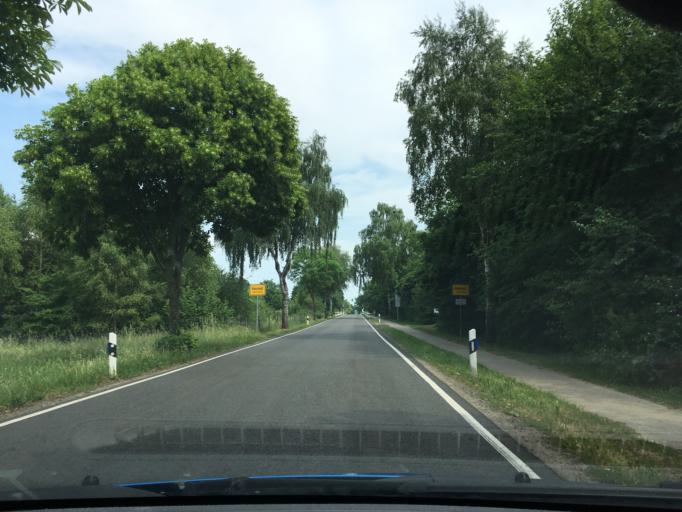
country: DE
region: Lower Saxony
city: Hanstedt
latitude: 53.2593
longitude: 10.0024
